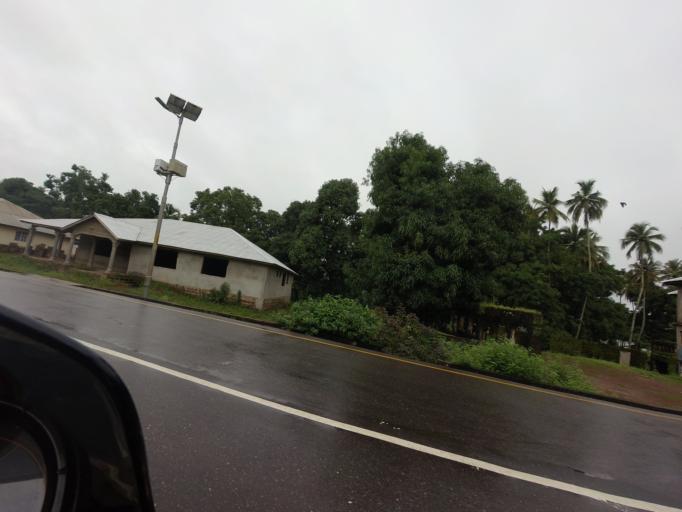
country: SL
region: Northern Province
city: Kambia
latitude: 9.1255
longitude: -12.9208
